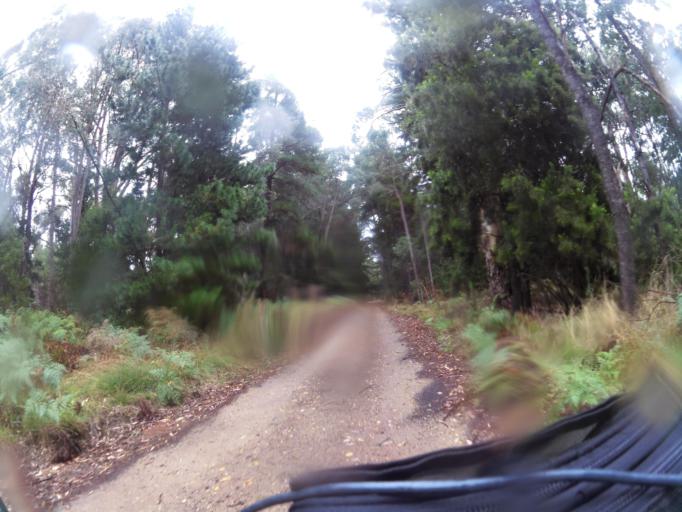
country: AU
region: New South Wales
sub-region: Greater Hume Shire
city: Holbrook
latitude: -36.1886
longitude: 147.5446
